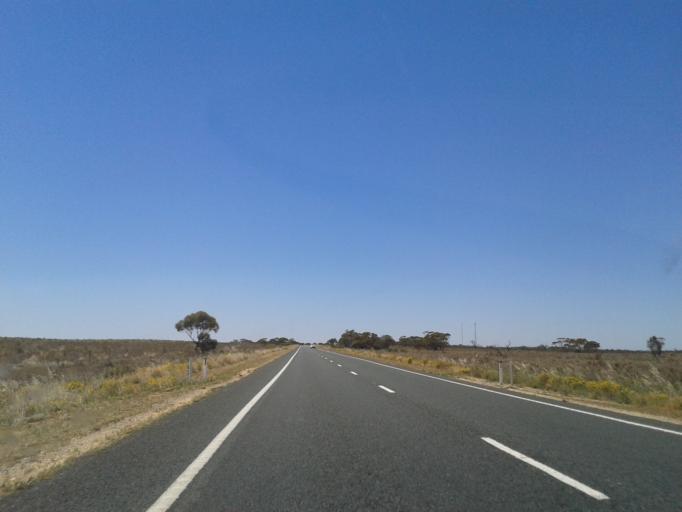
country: AU
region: New South Wales
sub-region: Wentworth
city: Gol Gol
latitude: -34.3186
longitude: 142.3750
